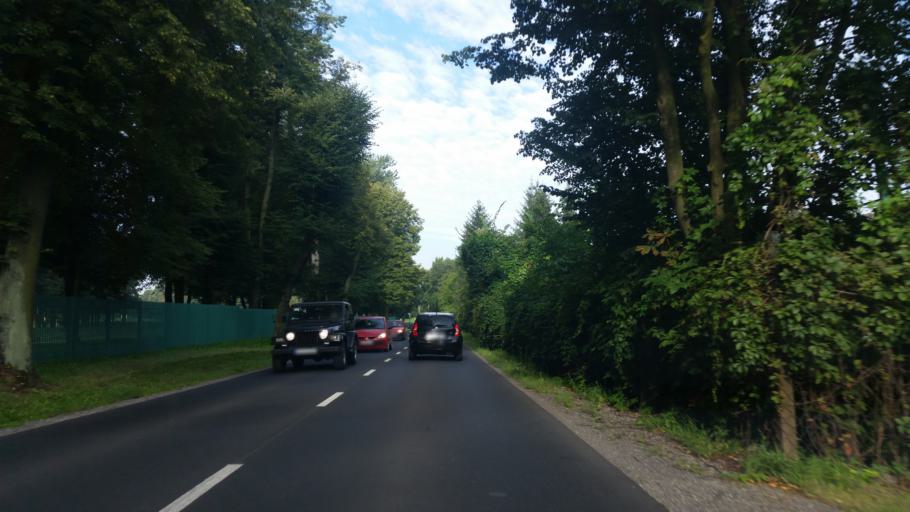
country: PL
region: Lesser Poland Voivodeship
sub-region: Powiat krakowski
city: Kryspinow
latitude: 50.0390
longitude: 19.8344
